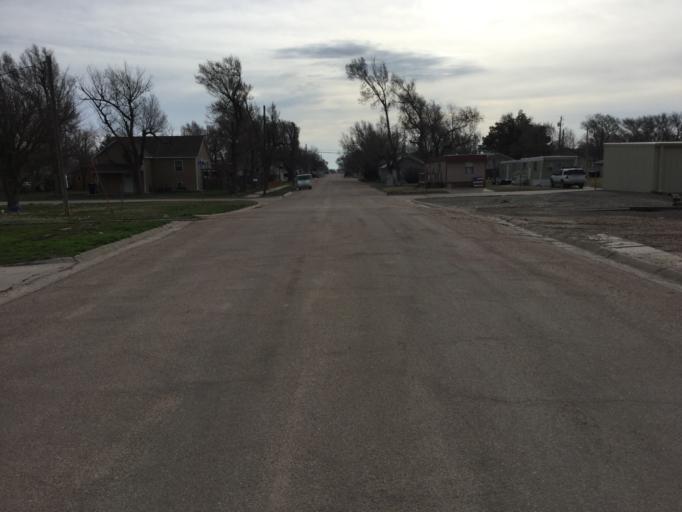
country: US
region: Kansas
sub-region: Scott County
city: Scott City
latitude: 38.4794
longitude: -100.9126
